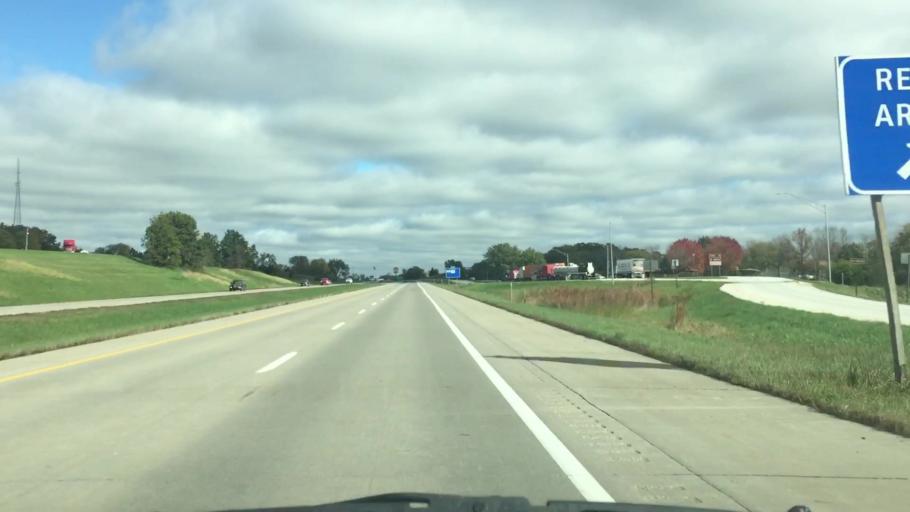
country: US
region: Iowa
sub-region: Clarke County
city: Osceola
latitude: 41.0113
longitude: -93.7965
